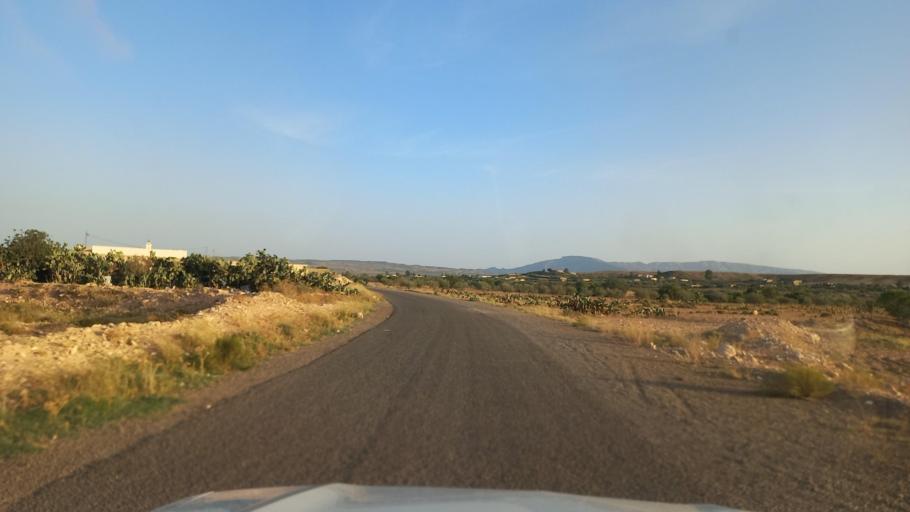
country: TN
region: Al Qasrayn
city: Kasserine
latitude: 35.2674
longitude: 8.9326
